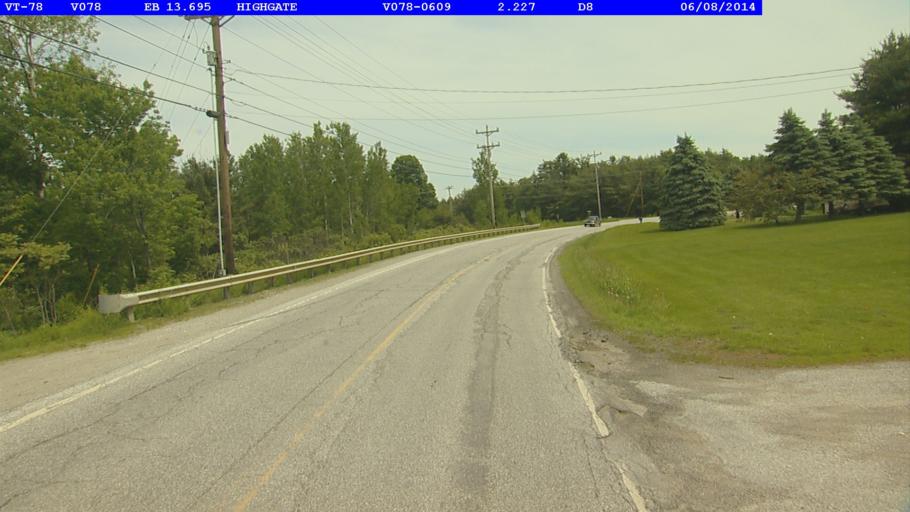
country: US
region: Vermont
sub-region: Franklin County
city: Swanton
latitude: 44.9415
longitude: -73.0612
